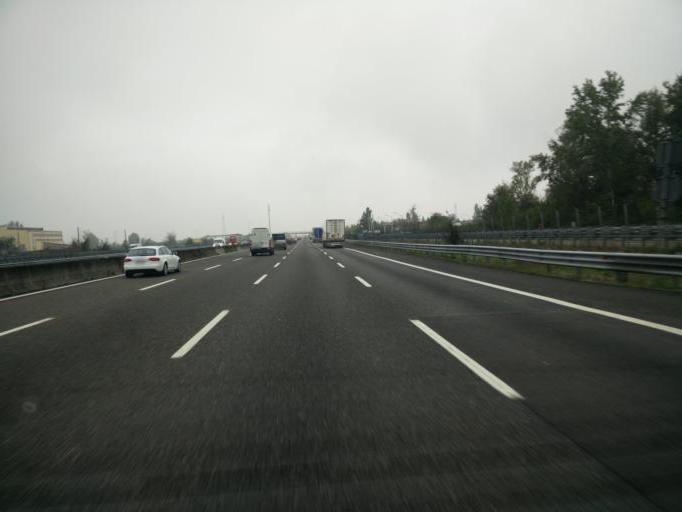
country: IT
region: Emilia-Romagna
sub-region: Provincia di Modena
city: Montale
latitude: 44.6060
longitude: 10.9143
